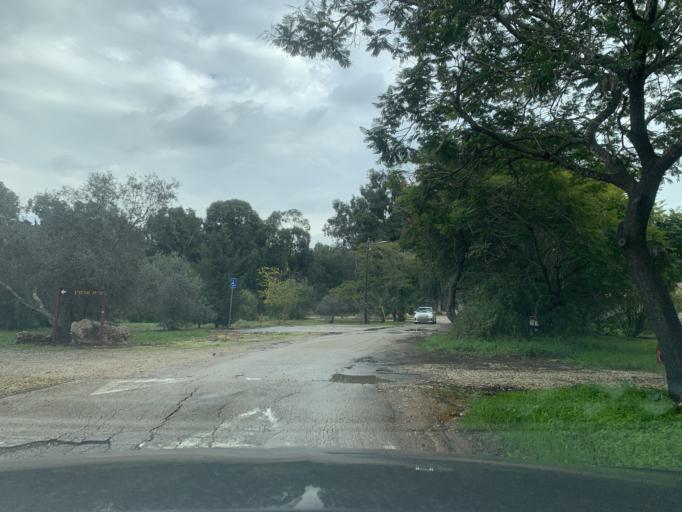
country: PS
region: West Bank
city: Qalqilyah
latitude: 32.2143
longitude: 34.9792
